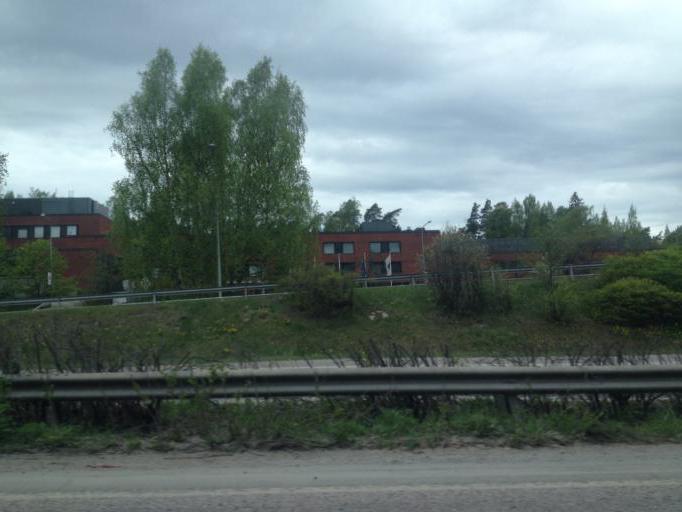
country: FI
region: Uusimaa
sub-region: Helsinki
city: Helsinki
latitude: 60.2181
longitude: 24.9086
